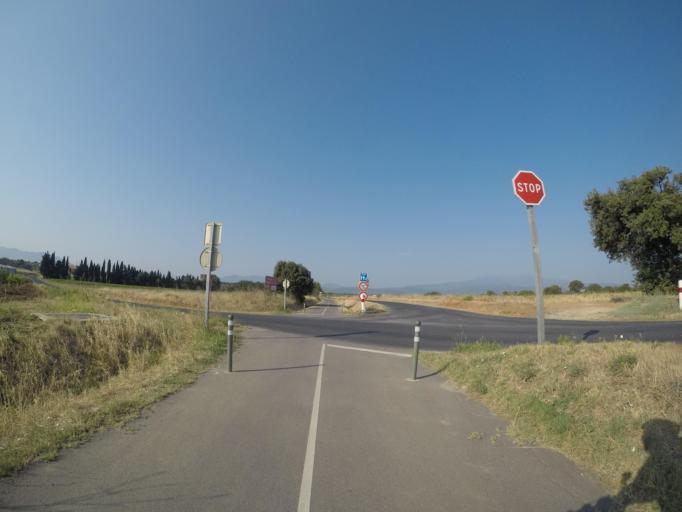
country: FR
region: Languedoc-Roussillon
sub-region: Departement des Pyrenees-Orientales
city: Ponteilla
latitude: 42.6348
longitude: 2.8083
